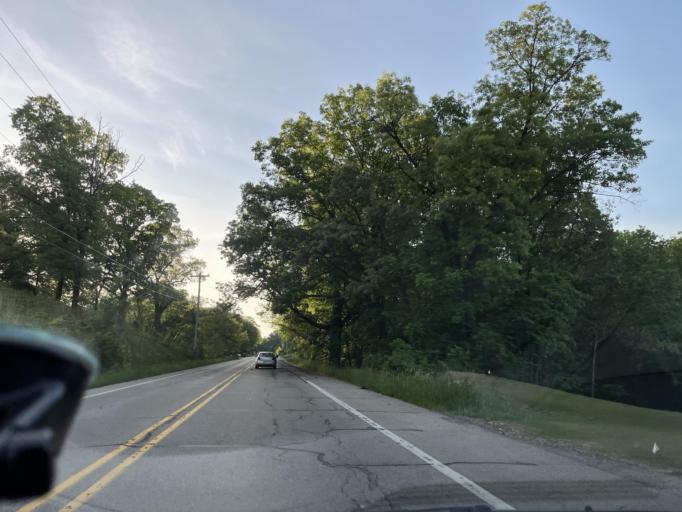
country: US
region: Michigan
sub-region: Barry County
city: Middleville
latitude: 42.7132
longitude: -85.4528
